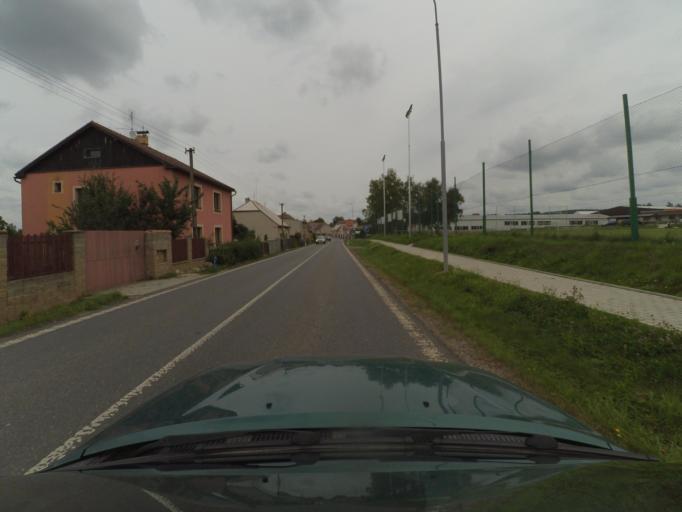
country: CZ
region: Central Bohemia
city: Pavlikov
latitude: 50.0735
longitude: 13.6956
